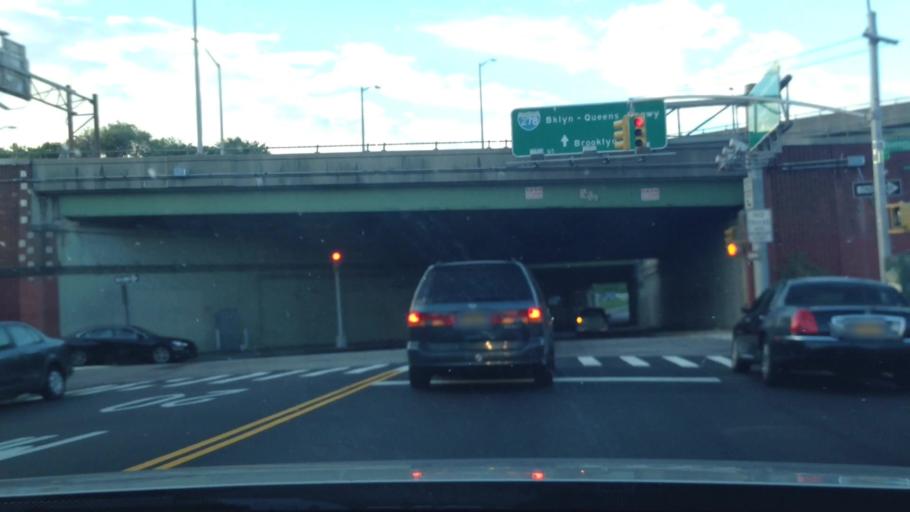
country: US
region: New York
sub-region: Queens County
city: Long Island City
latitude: 40.7359
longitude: -73.9230
